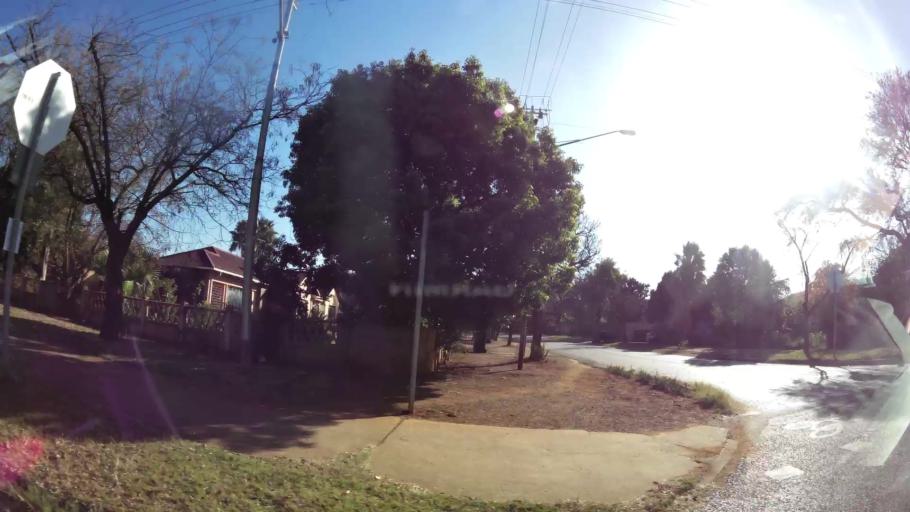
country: ZA
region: Gauteng
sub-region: City of Tshwane Metropolitan Municipality
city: Pretoria
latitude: -25.7061
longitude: 28.2614
